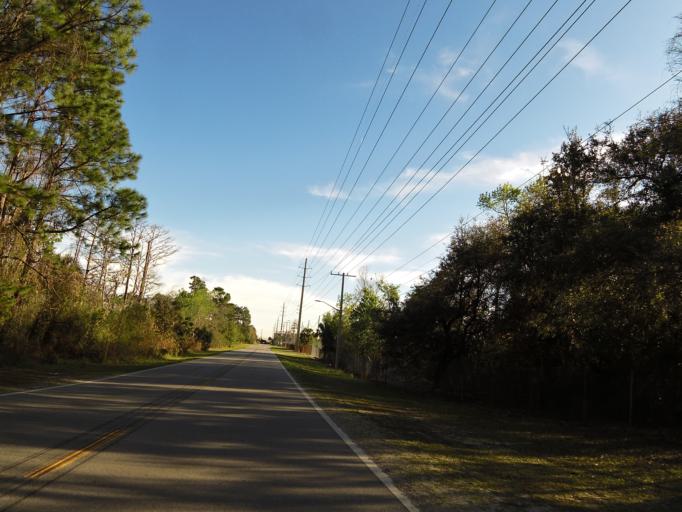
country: US
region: Florida
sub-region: Duval County
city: Jacksonville
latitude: 30.4273
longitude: -81.6022
